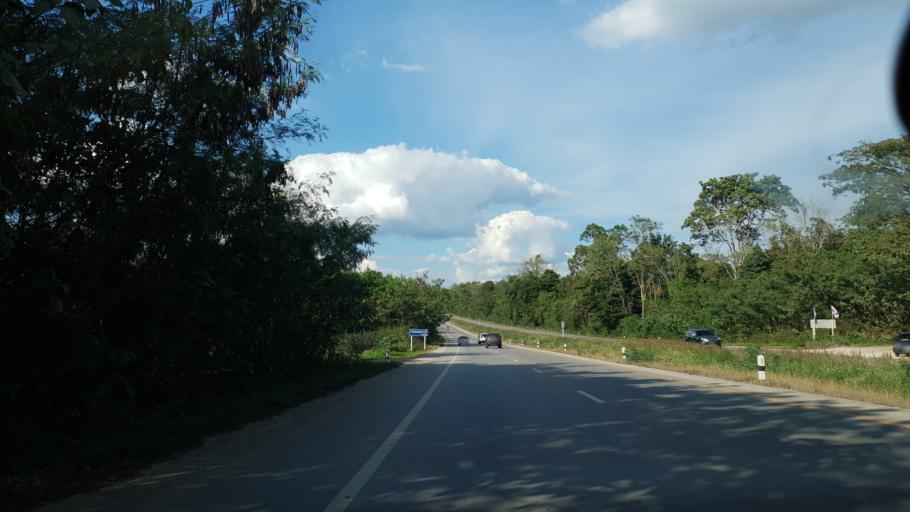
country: TH
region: Lampang
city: Mae Mo
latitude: 18.1988
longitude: 99.5914
